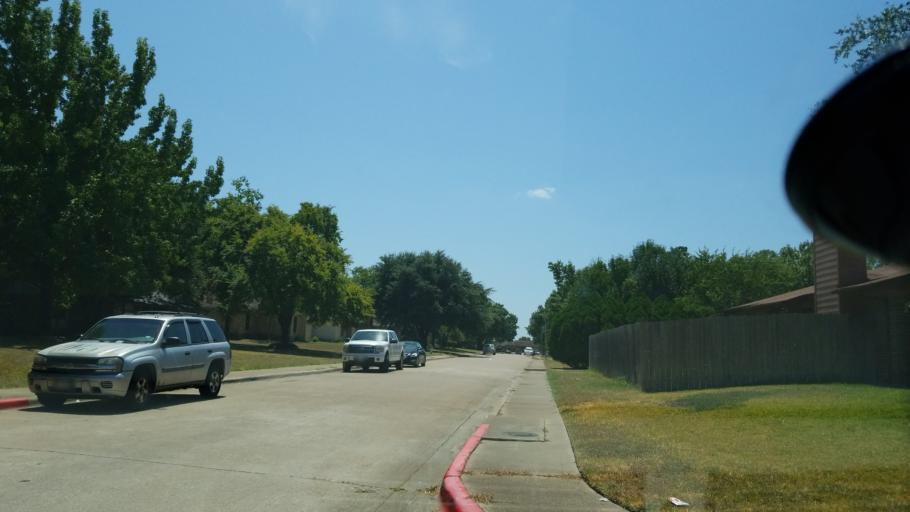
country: US
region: Texas
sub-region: Dallas County
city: Duncanville
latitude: 32.6358
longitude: -96.8842
